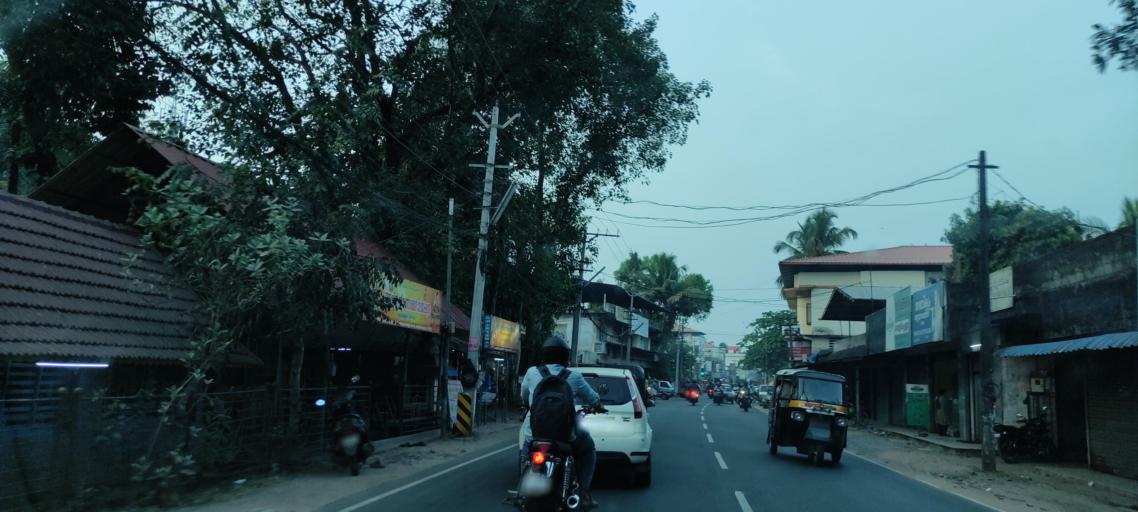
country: IN
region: Kerala
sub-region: Alappuzha
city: Mavelikara
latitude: 9.3182
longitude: 76.5336
